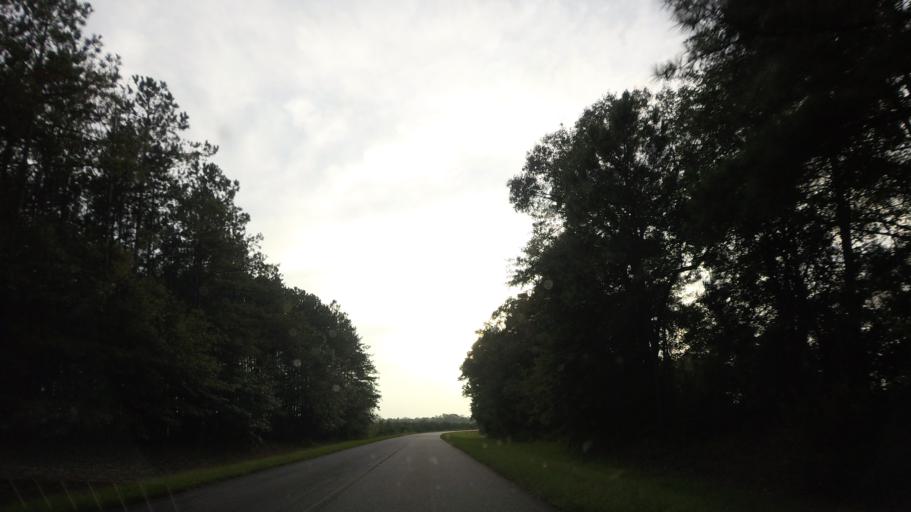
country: US
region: Georgia
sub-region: Wilkinson County
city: Gordon
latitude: 32.8681
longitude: -83.4798
